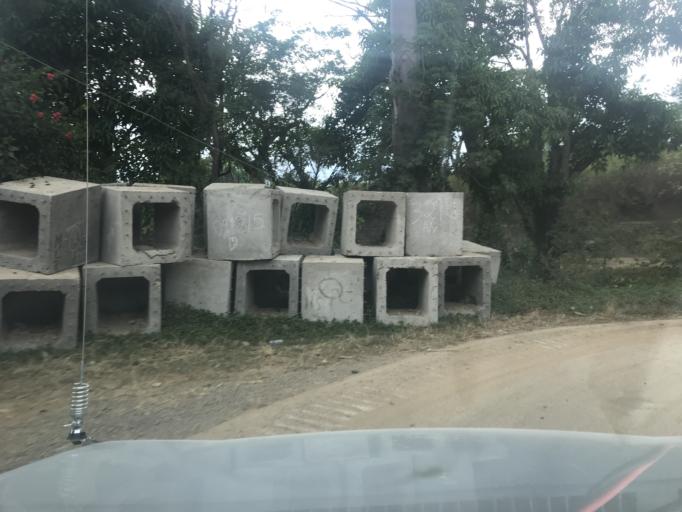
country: TL
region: Ainaro
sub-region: Ainaro
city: Ainaro
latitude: -8.9997
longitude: 125.5016
